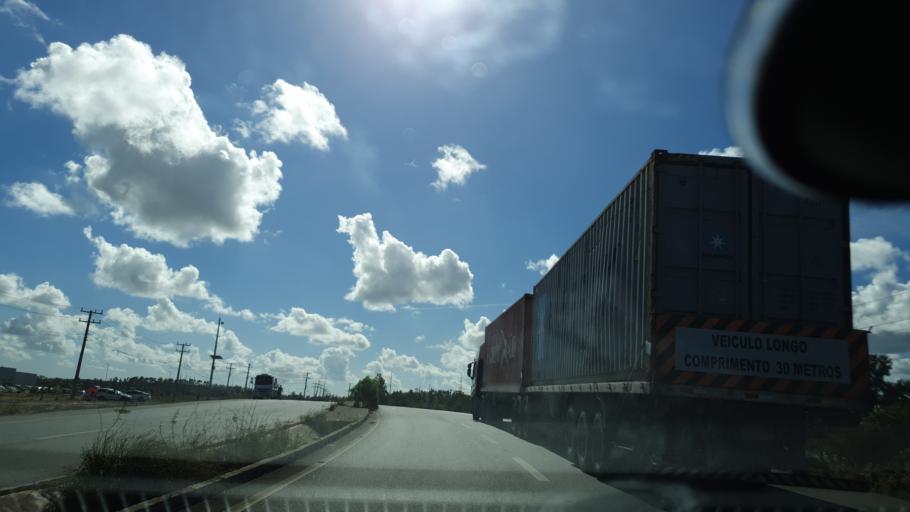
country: BR
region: Bahia
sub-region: Camacari
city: Camacari
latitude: -12.6834
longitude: -38.2664
